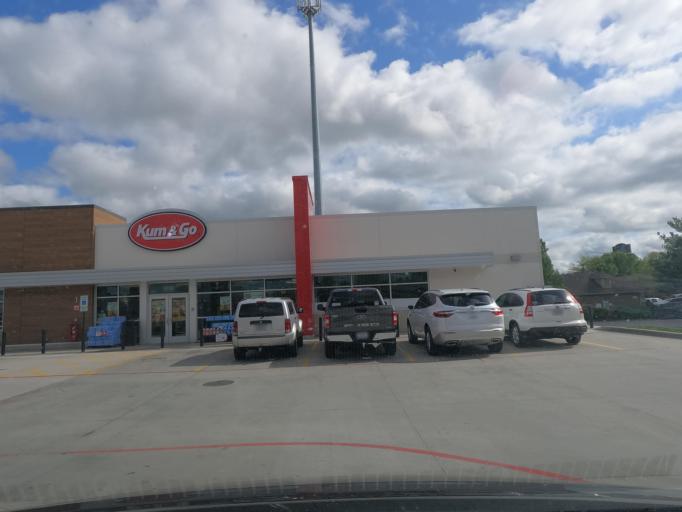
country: US
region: Missouri
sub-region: Greene County
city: Battlefield
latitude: 37.1378
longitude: -93.2977
